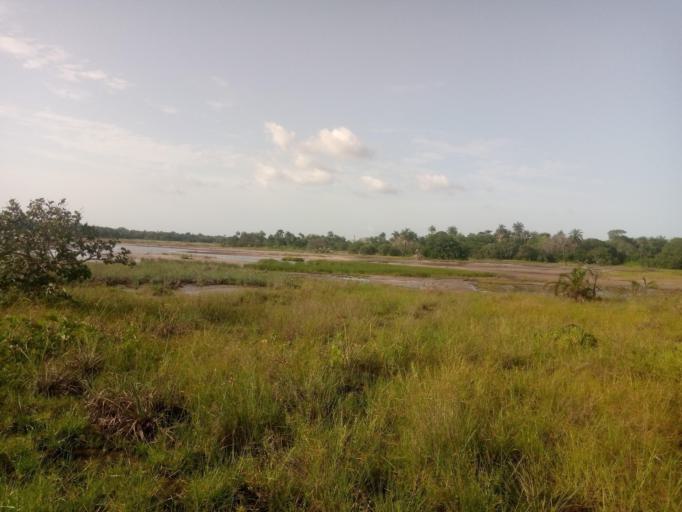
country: GM
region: Western
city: Gunjur
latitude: 13.0416
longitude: -16.7257
